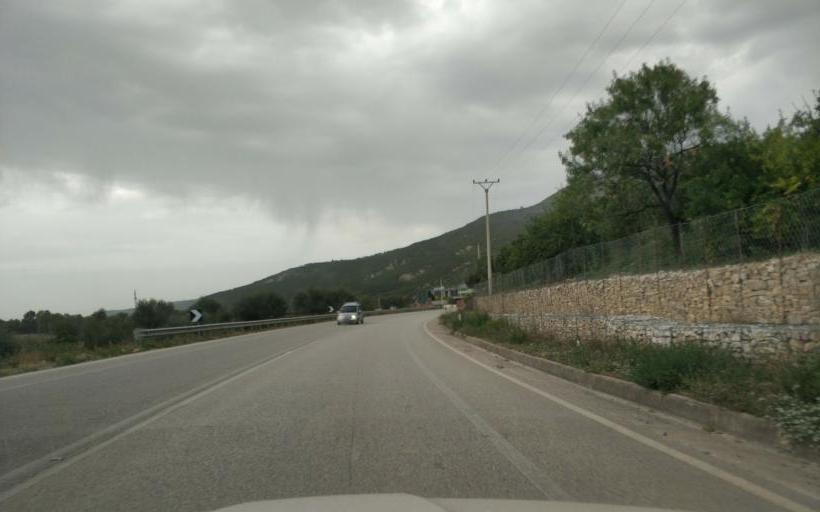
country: AL
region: Fier
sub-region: Rrethi i Mallakastres
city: Hekal
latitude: 40.5158
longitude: 19.7424
